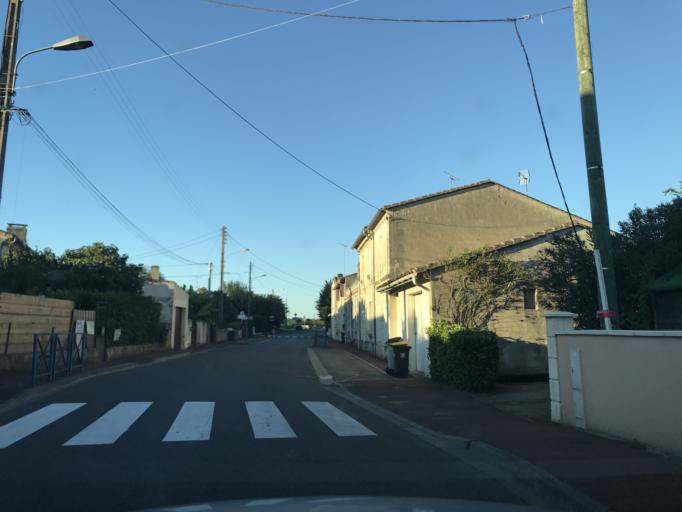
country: FR
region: Aquitaine
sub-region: Departement de la Gironde
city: Saint-Medard-de-Guizieres
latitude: 45.0183
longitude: -0.0558
